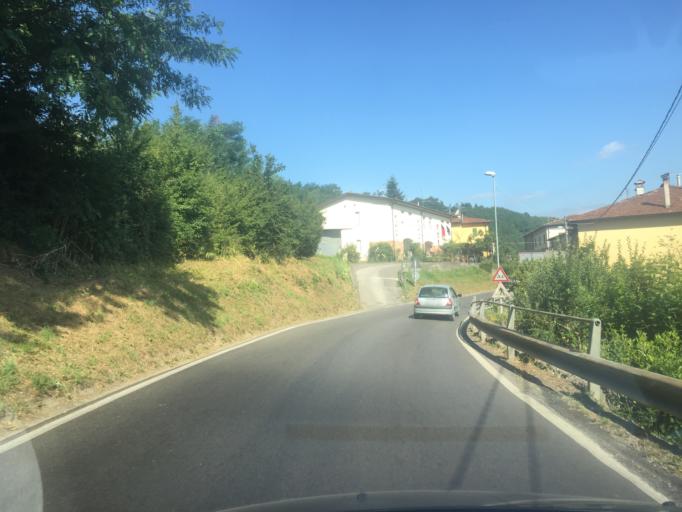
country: IT
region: Tuscany
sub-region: Provincia di Lucca
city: Villa Collemandina
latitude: 44.1331
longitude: 10.3733
